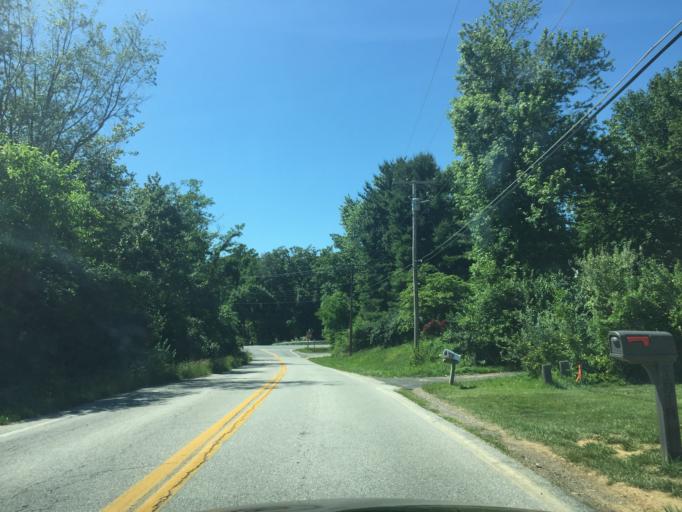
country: US
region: Maryland
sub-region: Carroll County
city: Manchester
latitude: 39.6275
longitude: -76.9319
